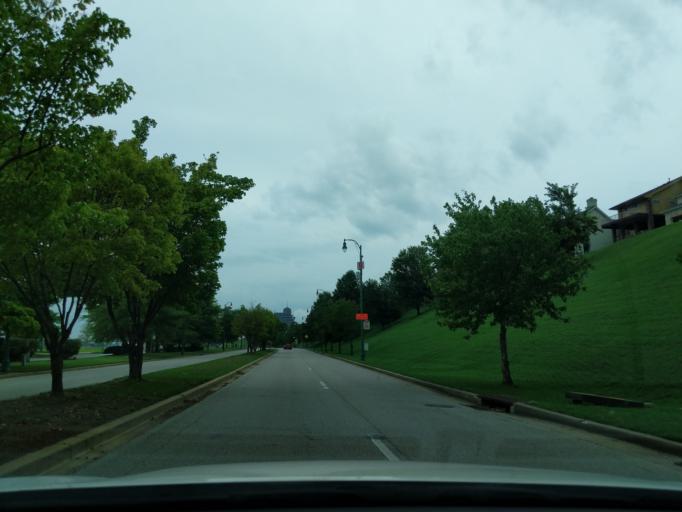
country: US
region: Tennessee
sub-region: Shelby County
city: Memphis
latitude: 35.1355
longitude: -90.0630
